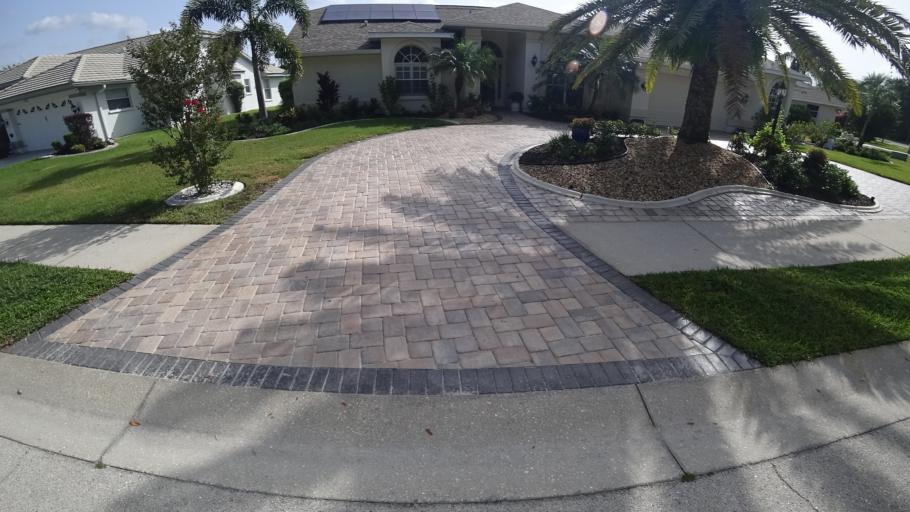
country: US
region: Florida
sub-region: Sarasota County
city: Desoto Lakes
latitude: 27.4329
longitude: -82.4790
